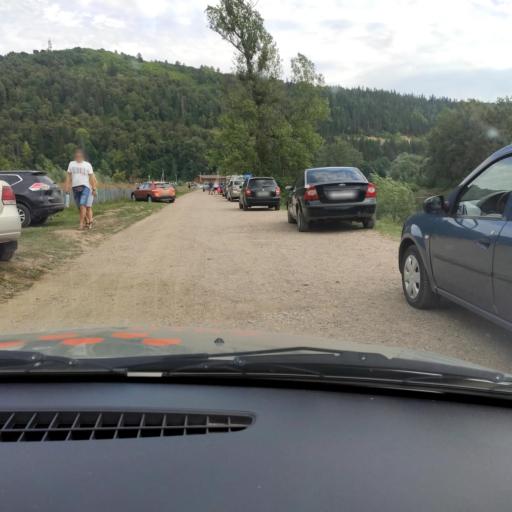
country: RU
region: Bashkortostan
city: Krasnyy Klyuch
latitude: 55.3784
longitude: 56.6745
